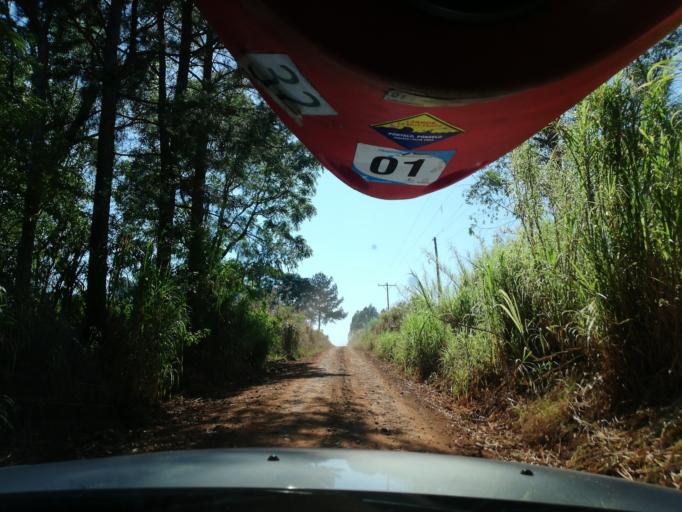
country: AR
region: Misiones
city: Puerto Leoni
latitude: -26.9689
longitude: -55.1568
